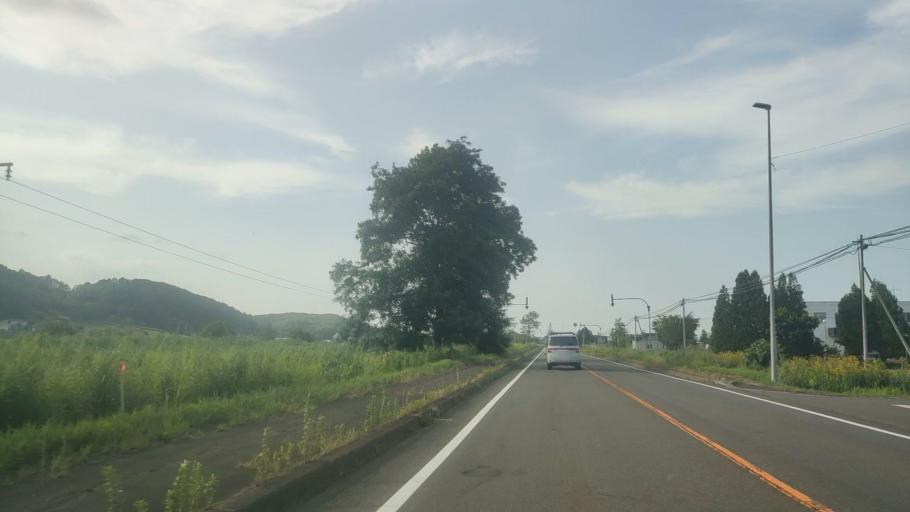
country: JP
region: Hokkaido
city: Iwamizawa
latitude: 43.0002
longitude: 141.7890
